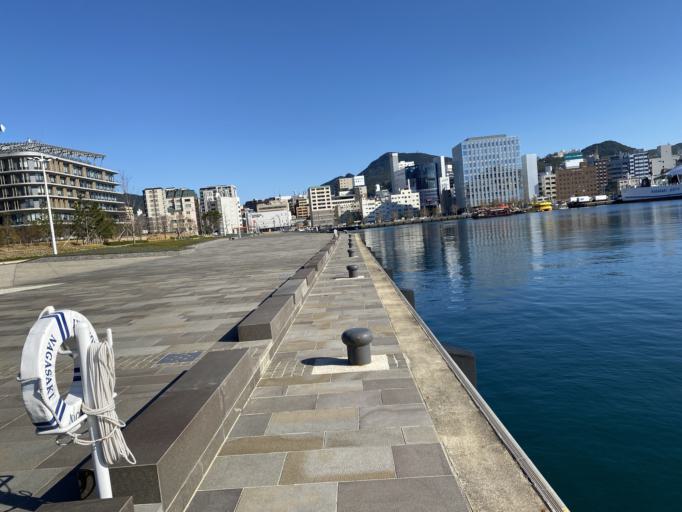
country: JP
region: Nagasaki
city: Nagasaki-shi
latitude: 32.7488
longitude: 129.8676
